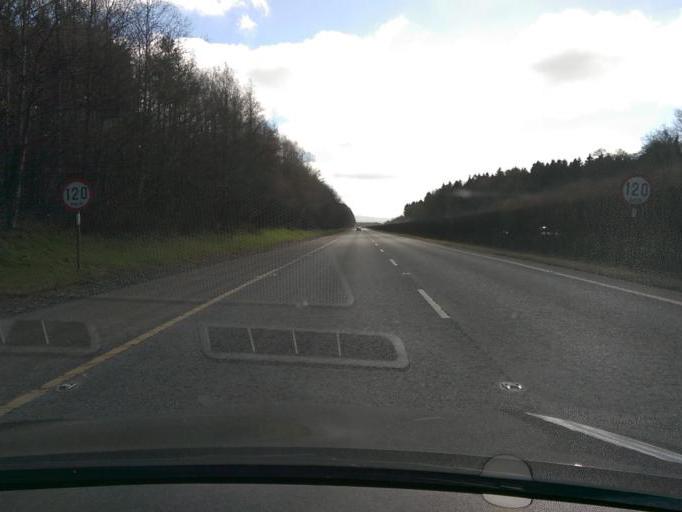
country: IE
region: Leinster
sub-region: Kildare
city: Kilcock
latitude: 53.3960
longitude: -6.6807
